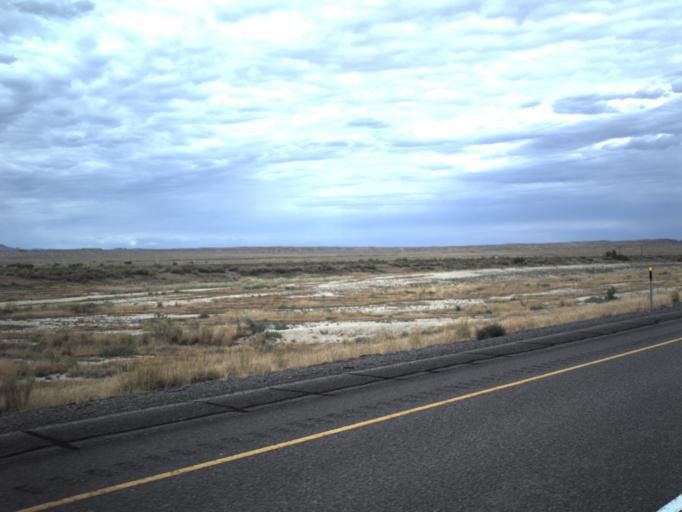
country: US
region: Utah
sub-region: Grand County
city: Moab
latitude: 38.9418
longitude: -109.5686
